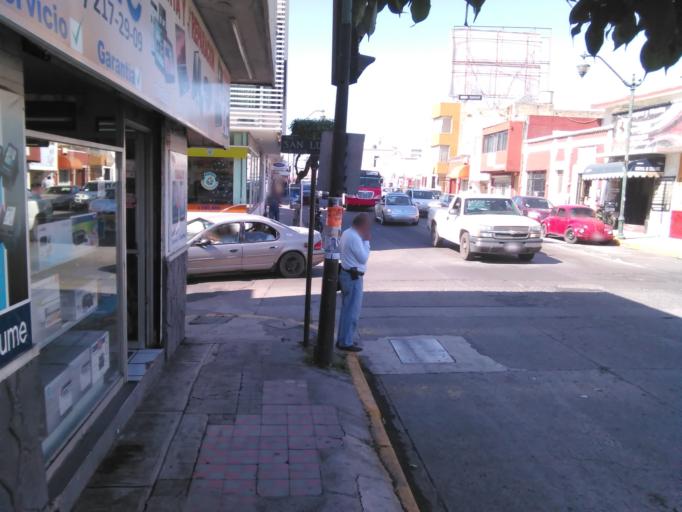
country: MX
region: Nayarit
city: Tepic
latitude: 21.5079
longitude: -104.8912
